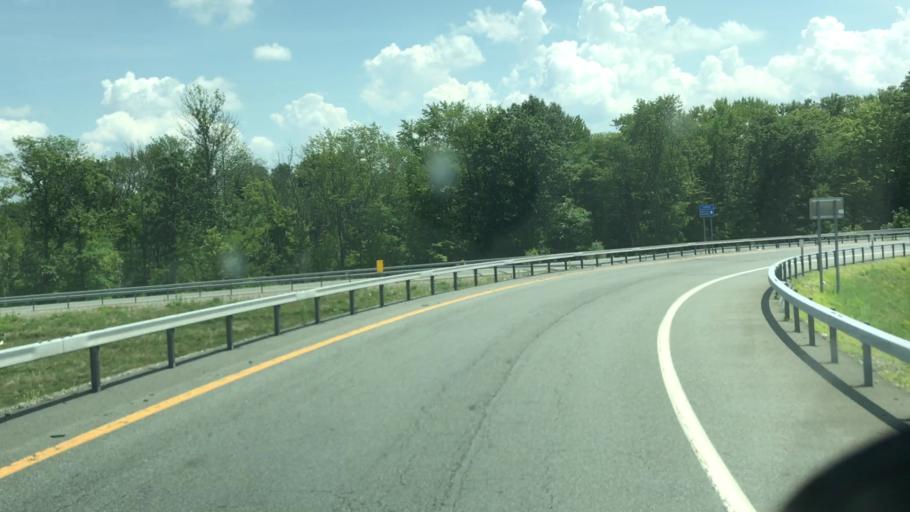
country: US
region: New York
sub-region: Orange County
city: Maybrook
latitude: 41.5111
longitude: -74.2049
